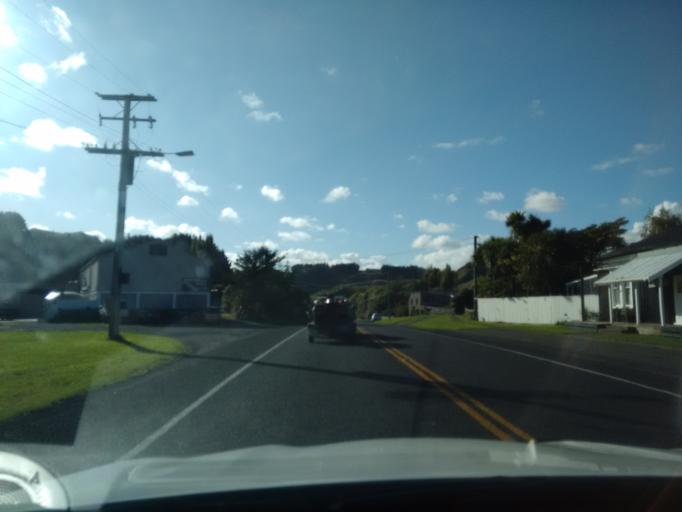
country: NZ
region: Manawatu-Wanganui
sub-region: Wanganui District
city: Wanganui
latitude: -39.8481
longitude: 174.9275
